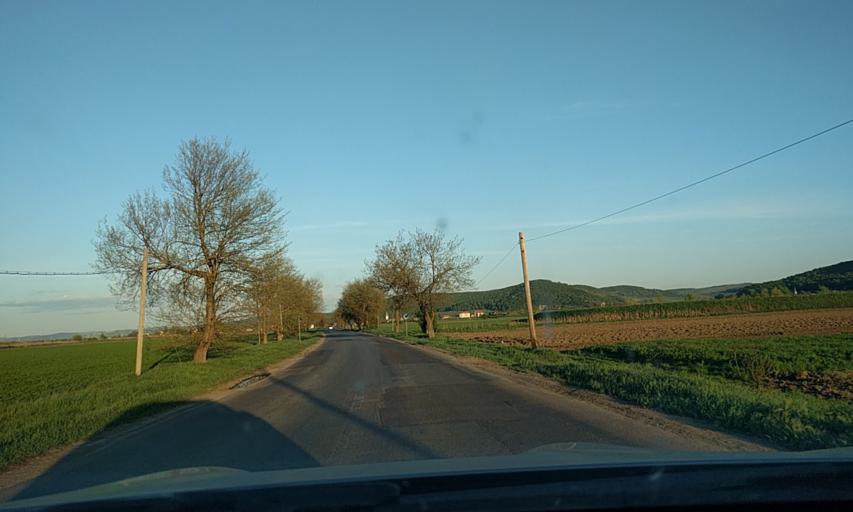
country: RO
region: Mures
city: Gheorghe Doja
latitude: 46.4704
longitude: 24.4940
